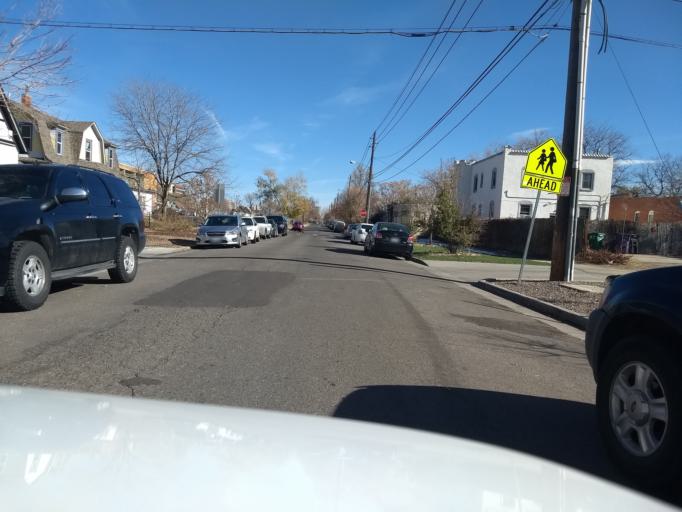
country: US
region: Colorado
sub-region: Denver County
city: Denver
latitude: 39.7241
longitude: -104.9960
